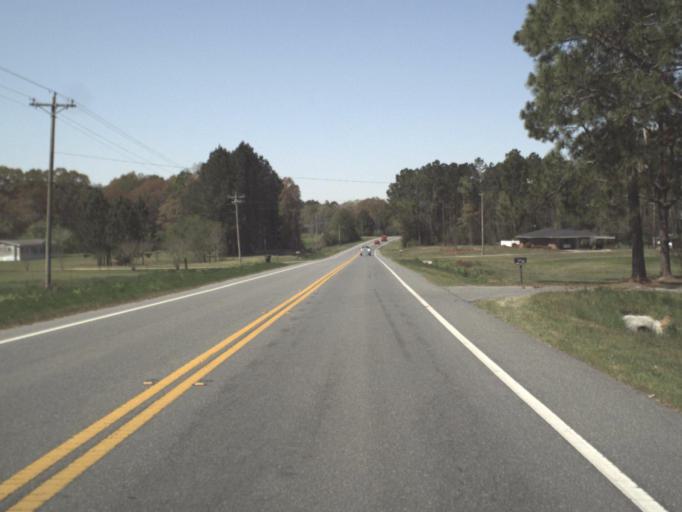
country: US
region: Florida
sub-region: Jackson County
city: Graceville
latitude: 30.9631
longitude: -85.5866
